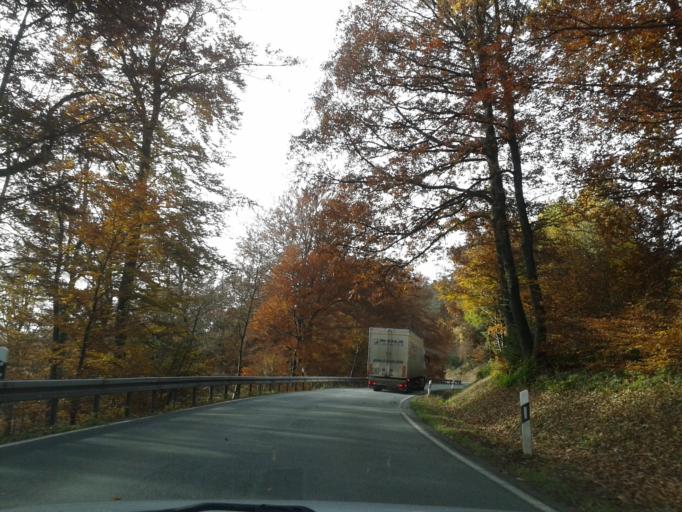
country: DE
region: North Rhine-Westphalia
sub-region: Regierungsbezirk Arnsberg
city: Bestwig
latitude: 51.4014
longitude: 8.4206
